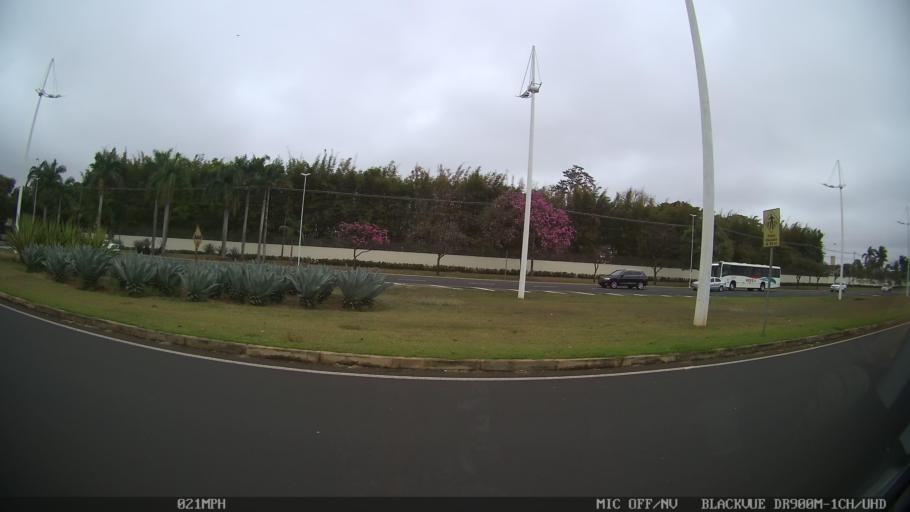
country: BR
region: Sao Paulo
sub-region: Sao Jose Do Rio Preto
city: Sao Jose do Rio Preto
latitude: -20.8483
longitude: -49.4035
